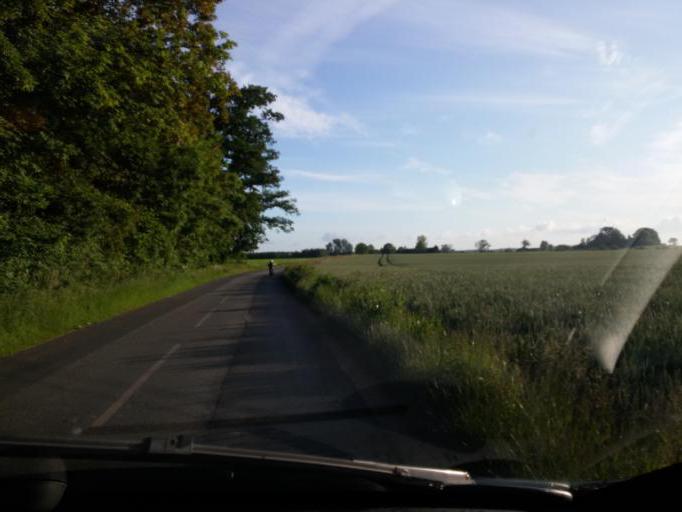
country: DK
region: South Denmark
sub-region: Kerteminde Kommune
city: Munkebo
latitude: 55.4286
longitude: 10.5392
